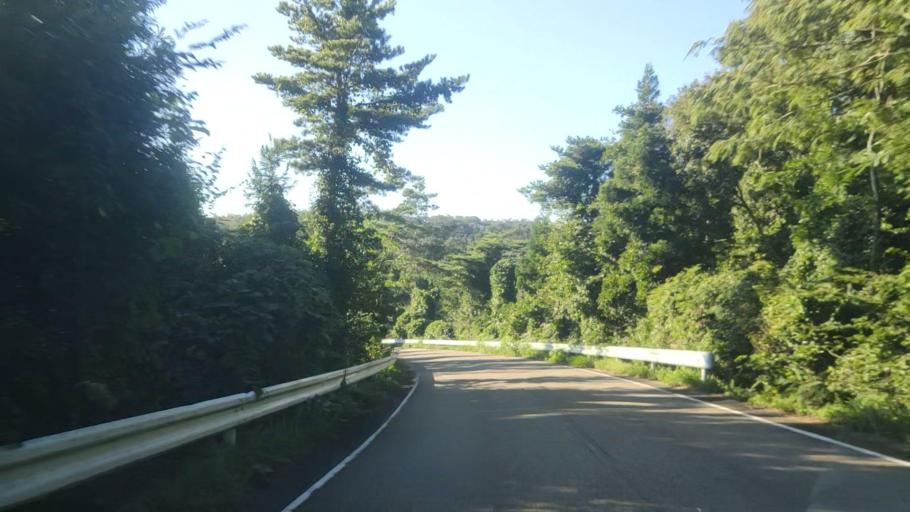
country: JP
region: Ishikawa
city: Nanao
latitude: 37.1196
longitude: 136.9449
